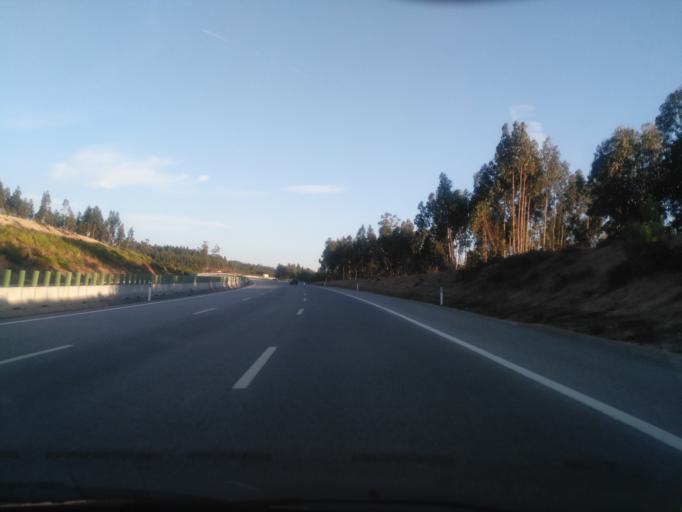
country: PT
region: Coimbra
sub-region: Figueira da Foz
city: Alhadas
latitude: 40.1163
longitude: -8.7478
